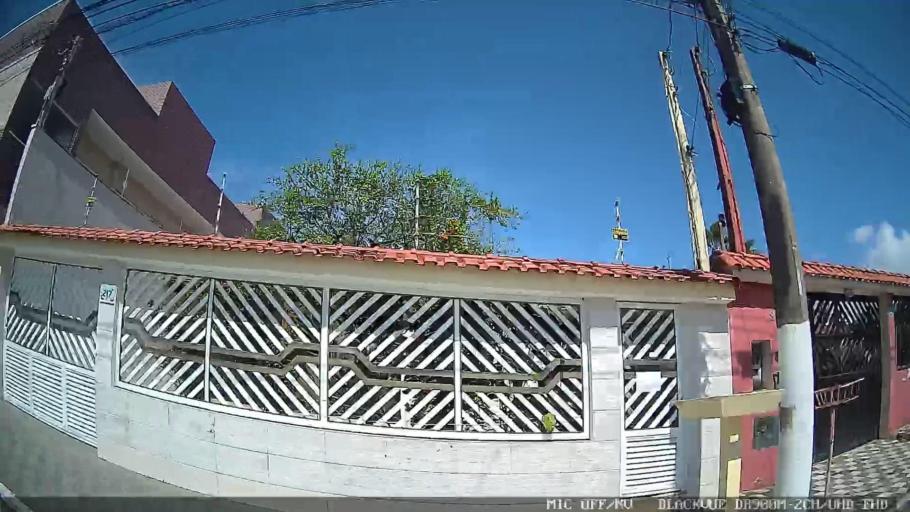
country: BR
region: Sao Paulo
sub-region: Peruibe
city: Peruibe
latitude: -24.3193
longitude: -46.9927
